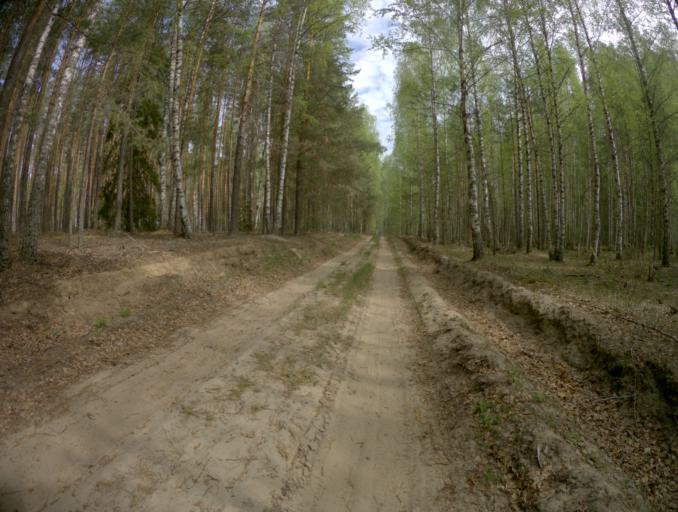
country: RU
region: Ivanovo
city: Yuzha
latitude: 56.4877
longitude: 42.1558
